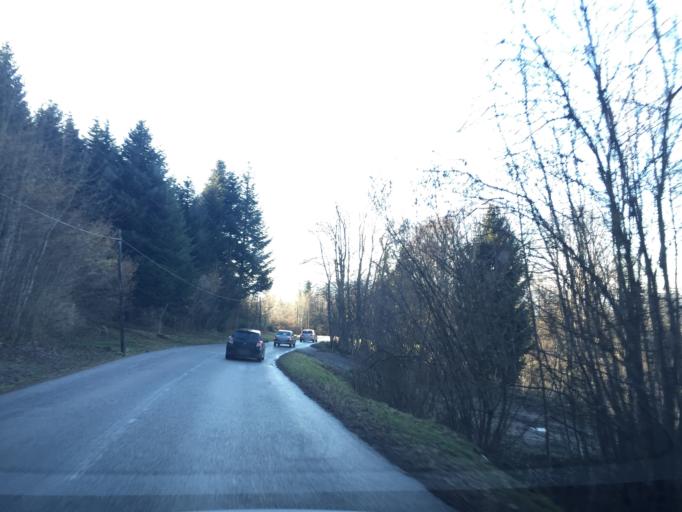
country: FR
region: Rhone-Alpes
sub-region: Departement de la Savoie
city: Mouxy
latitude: 45.6997
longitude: 5.9773
